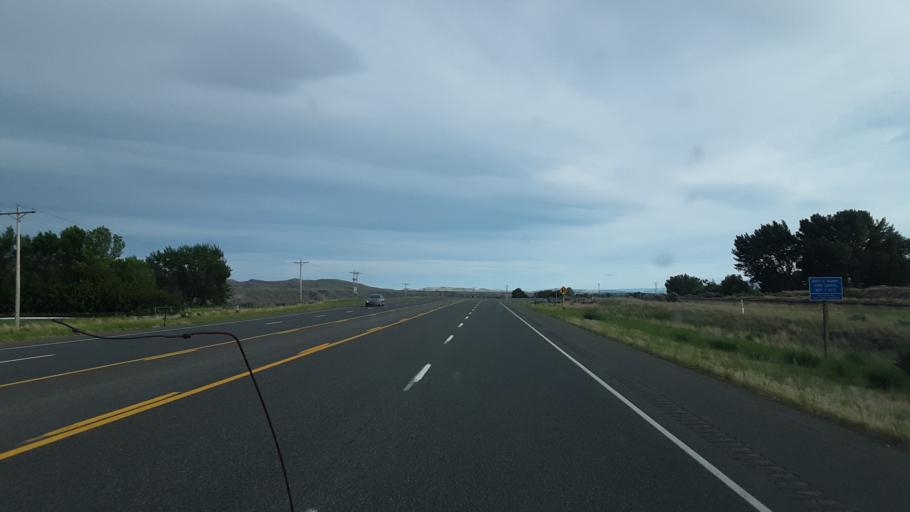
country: US
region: Wyoming
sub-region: Park County
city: Cody
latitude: 44.6275
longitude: -108.9560
